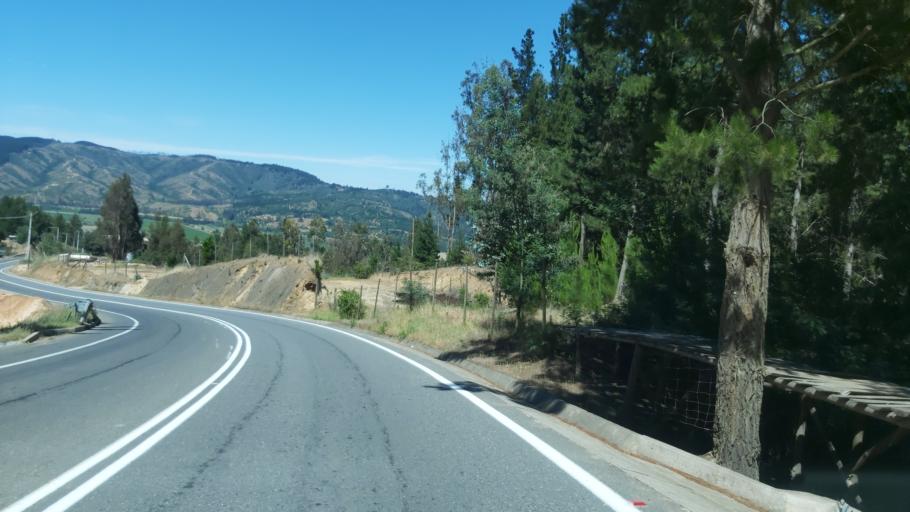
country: CL
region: Maule
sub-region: Provincia de Talca
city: Talca
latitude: -34.9800
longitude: -71.9723
